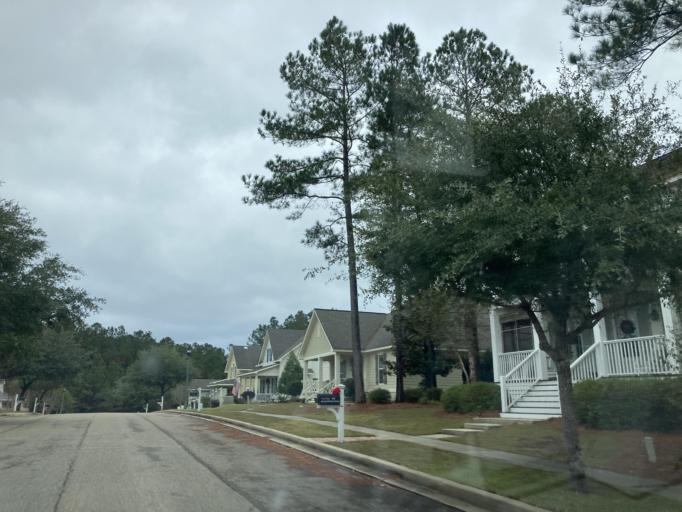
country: US
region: Mississippi
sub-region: Lamar County
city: West Hattiesburg
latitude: 31.2835
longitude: -89.4728
